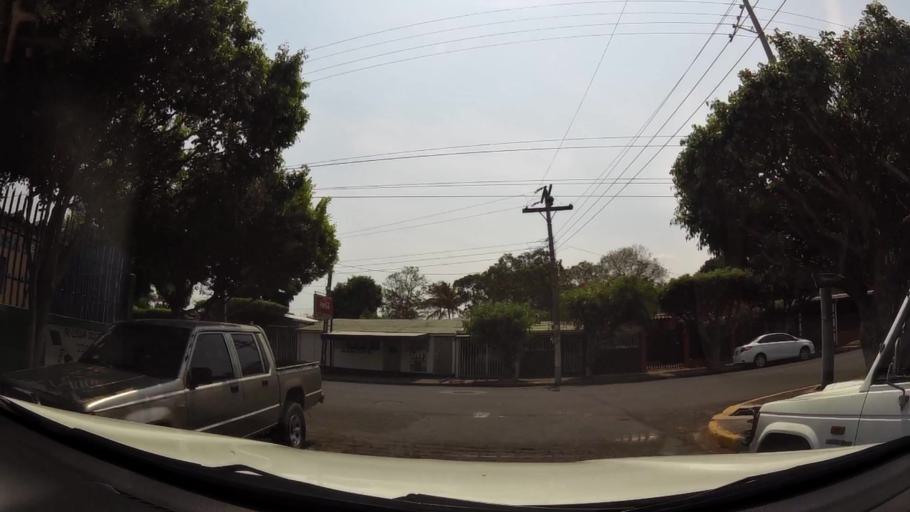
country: NI
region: Managua
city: Ciudad Sandino
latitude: 12.1537
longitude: -86.3126
